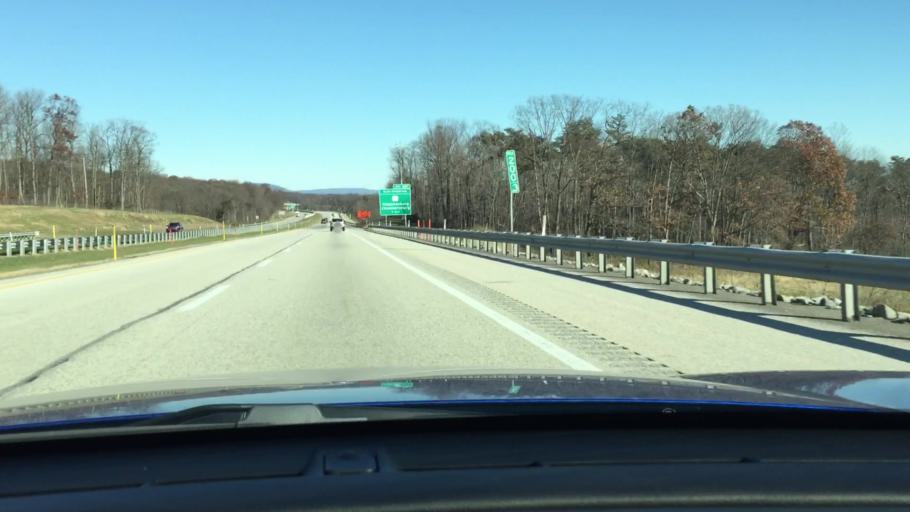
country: US
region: Pennsylvania
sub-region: Franklin County
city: Doylestown
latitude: 40.1512
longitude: -77.6302
